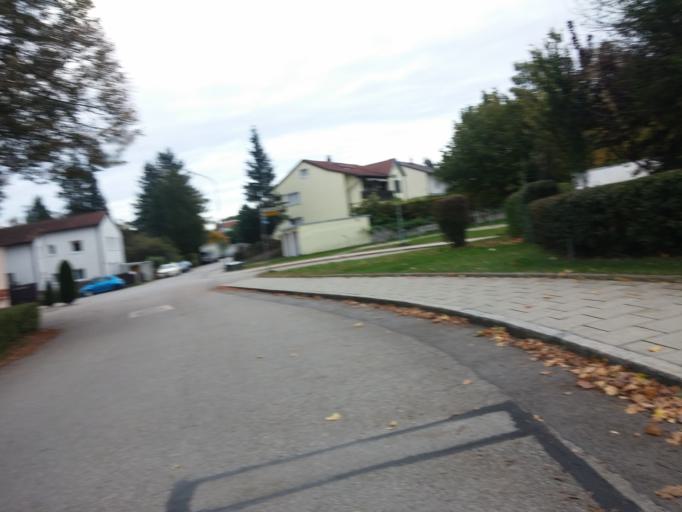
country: DE
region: Bavaria
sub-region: Upper Bavaria
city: Kirchseeon
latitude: 48.0748
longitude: 11.8813
